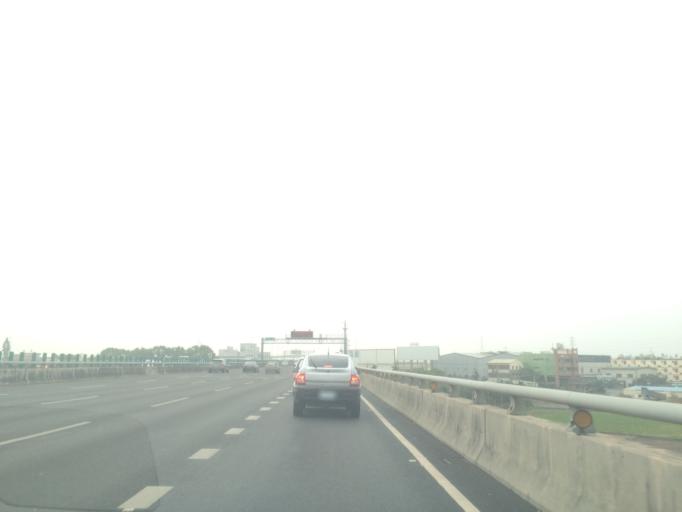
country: TW
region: Taiwan
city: Zhongxing New Village
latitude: 24.0354
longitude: 120.6745
